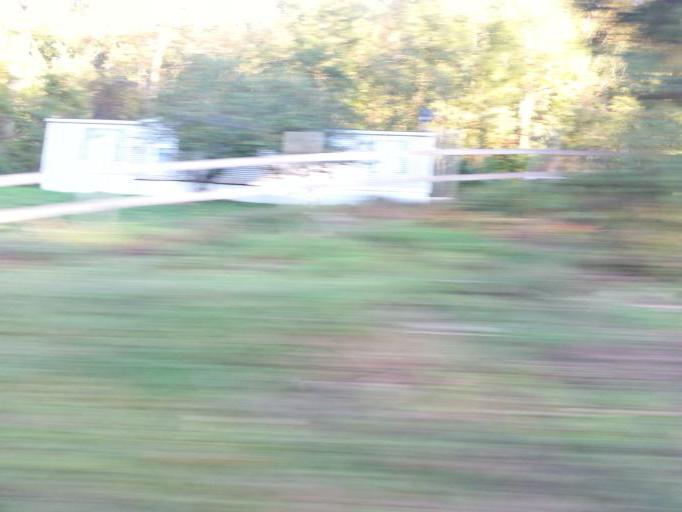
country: US
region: Tennessee
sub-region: Knox County
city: Knoxville
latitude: 36.0504
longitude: -83.9392
